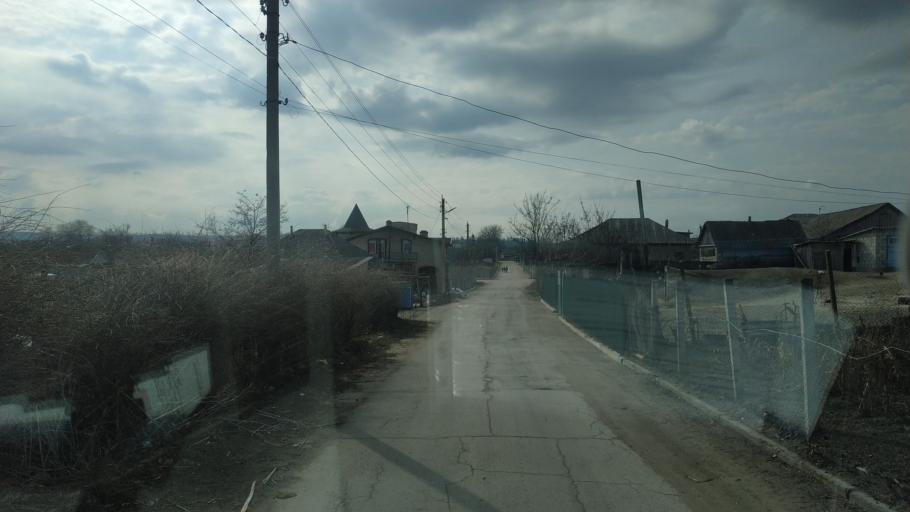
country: MD
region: Anenii Noi
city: Anenii Noi
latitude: 46.9049
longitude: 29.1413
